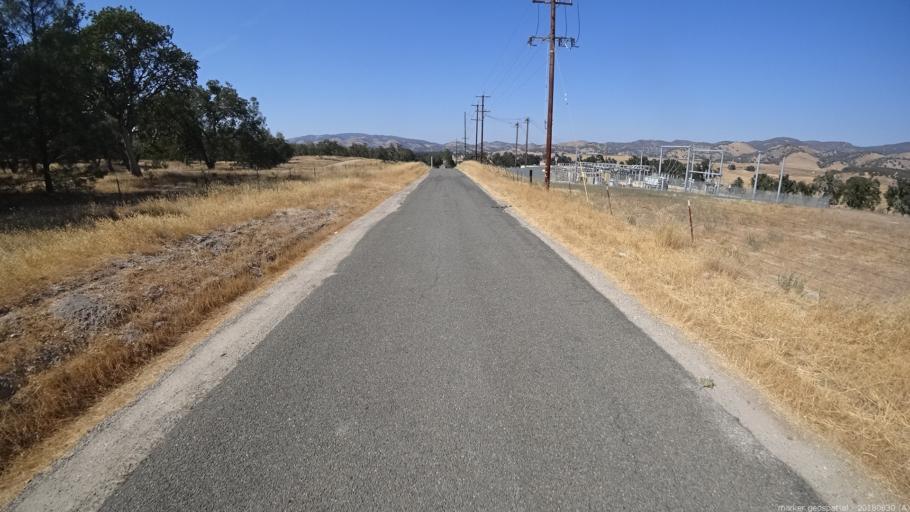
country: US
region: California
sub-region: Monterey County
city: King City
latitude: 36.0126
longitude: -121.1682
